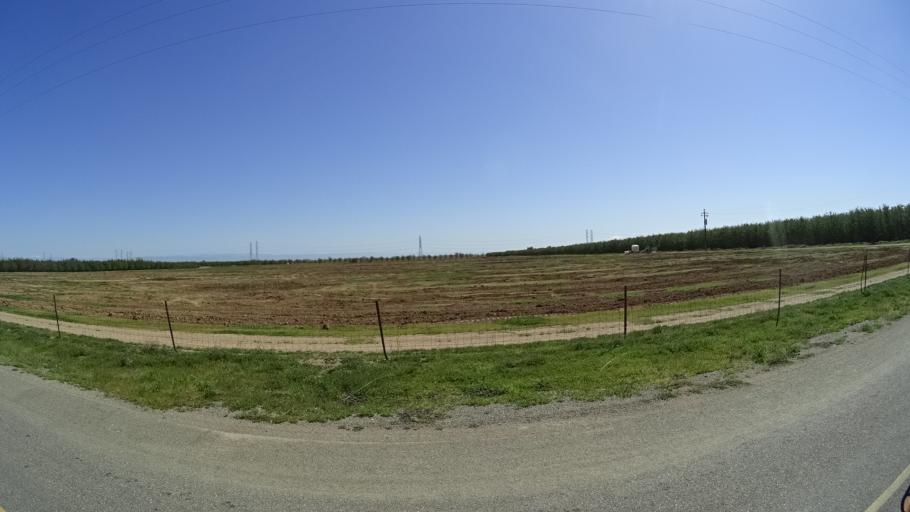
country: US
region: California
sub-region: Glenn County
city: Orland
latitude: 39.6875
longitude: -122.2716
